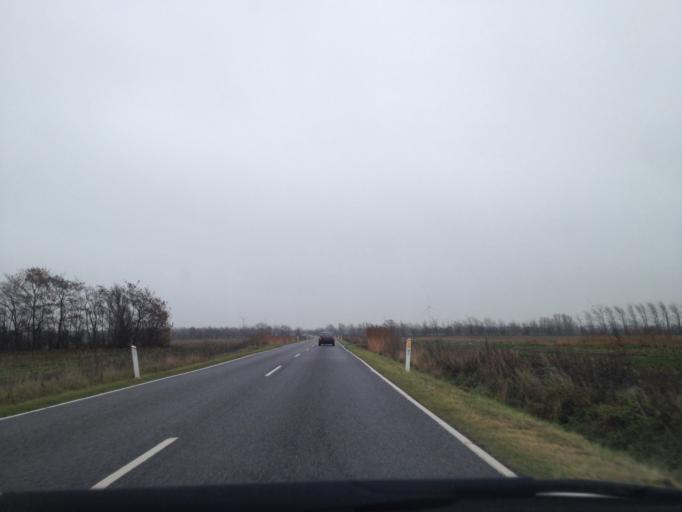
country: DK
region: South Denmark
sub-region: Tonder Kommune
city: Sherrebek
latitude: 55.0700
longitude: 8.7327
